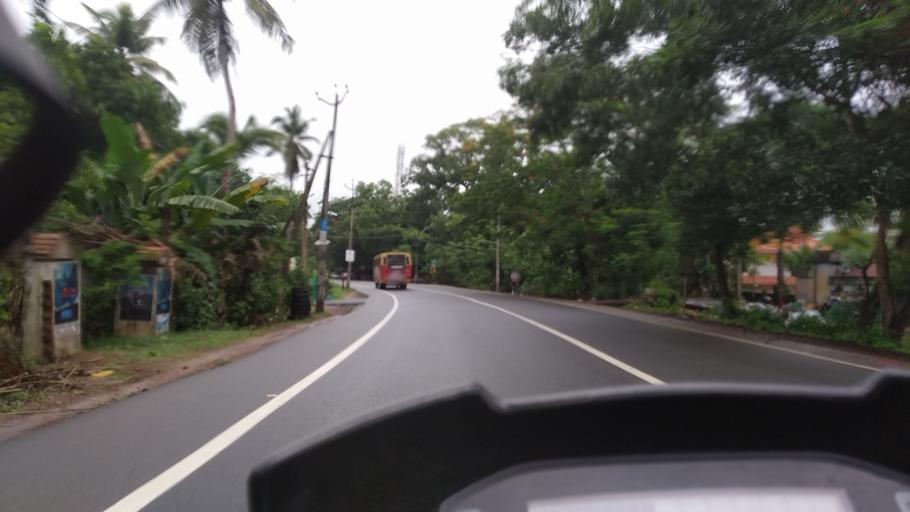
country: IN
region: Kerala
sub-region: Alappuzha
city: Mavelikara
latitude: 9.2872
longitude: 76.4389
